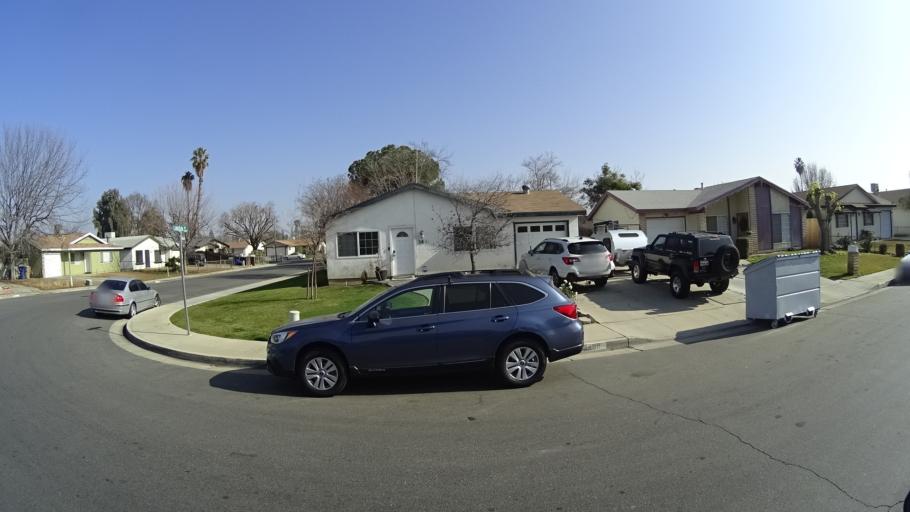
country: US
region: California
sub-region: Kern County
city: Bakersfield
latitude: 35.3238
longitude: -119.0610
